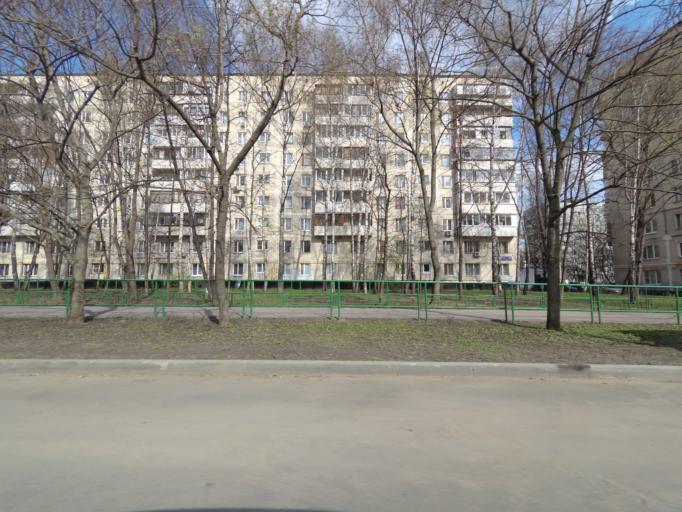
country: RU
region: Moscow
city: Gol'yanovo
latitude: 55.8223
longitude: 37.8257
